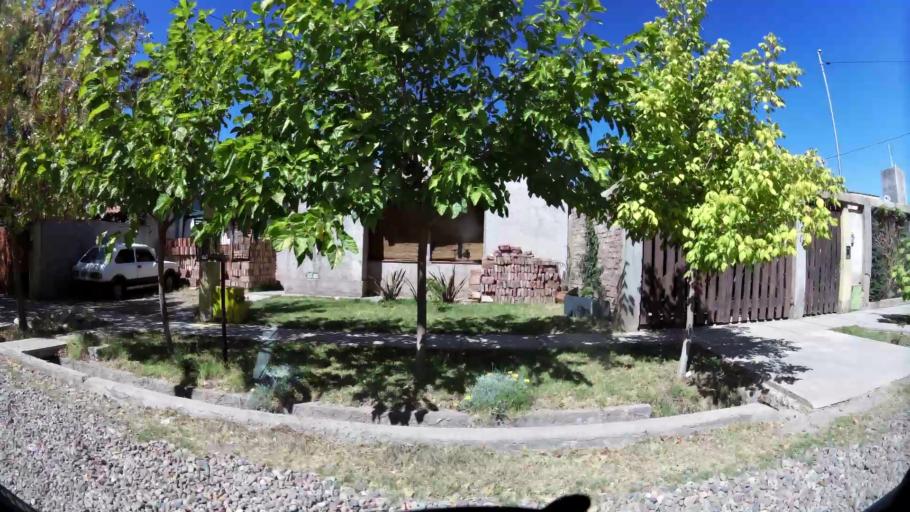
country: AR
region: Mendoza
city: Lujan de Cuyo
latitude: -32.9860
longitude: -68.8566
